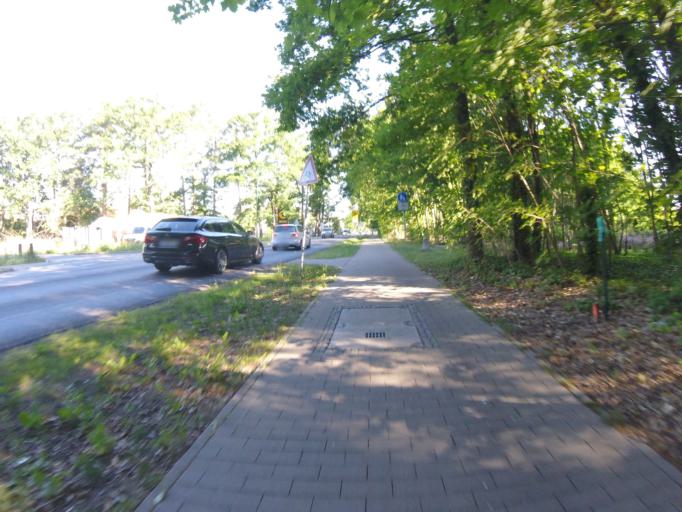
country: DE
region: Brandenburg
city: Konigs Wusterhausen
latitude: 52.2871
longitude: 13.6300
